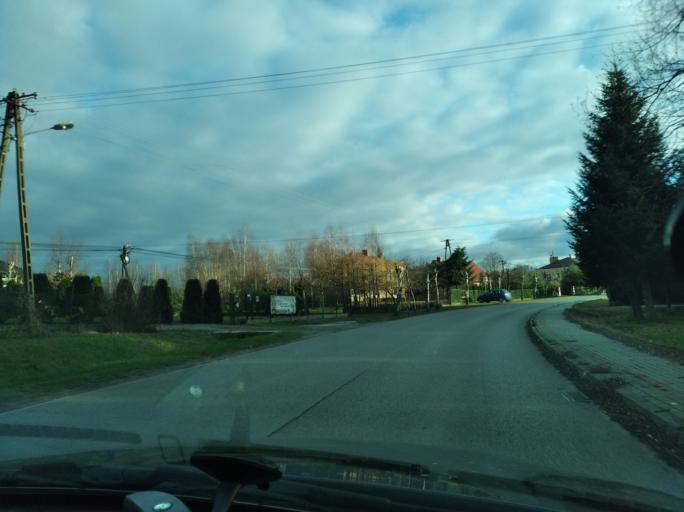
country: PL
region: Subcarpathian Voivodeship
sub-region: Powiat rzeszowski
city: Krasne
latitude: 50.0556
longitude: 22.1214
